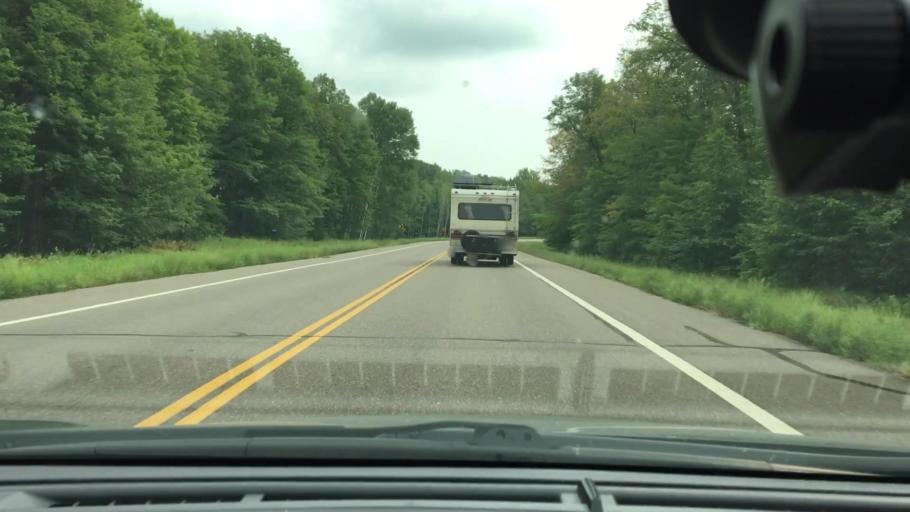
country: US
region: Minnesota
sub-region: Crow Wing County
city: Crosby
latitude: 46.4119
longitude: -93.8295
